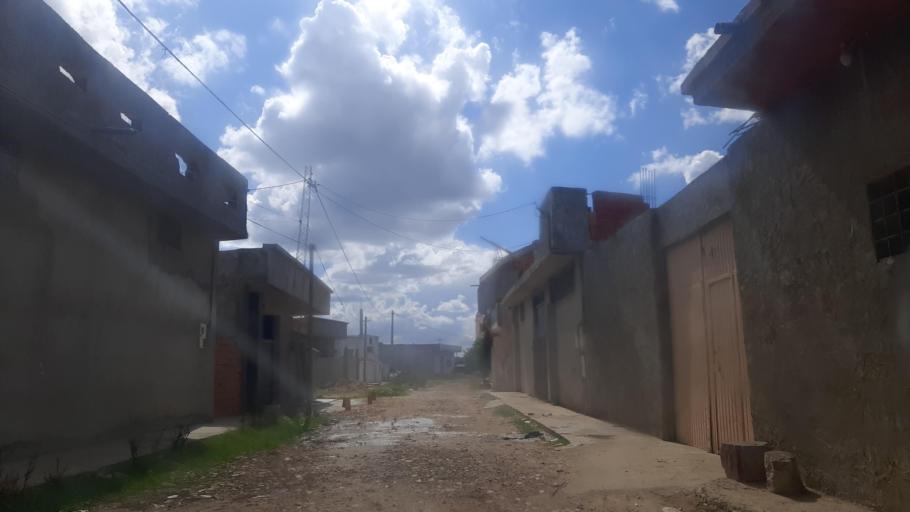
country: TN
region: Nabul
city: Korba
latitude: 36.5905
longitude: 10.8562
